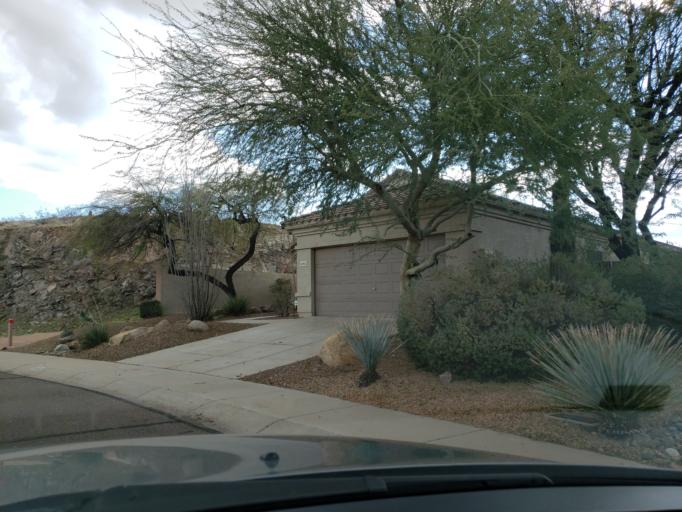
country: US
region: Arizona
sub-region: Maricopa County
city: Laveen
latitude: 33.2942
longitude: -112.0678
